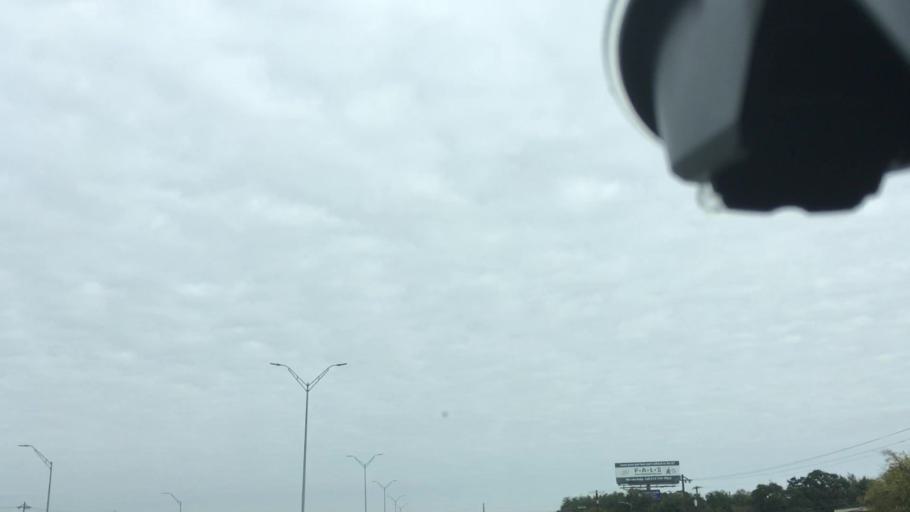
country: US
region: Texas
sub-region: Hays County
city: San Marcos
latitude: 29.8966
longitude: -97.9089
